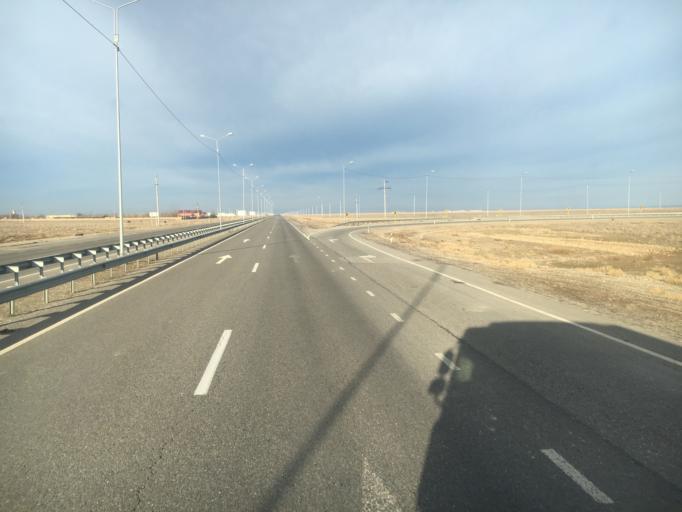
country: KZ
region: Ongtustik Qazaqstan
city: Turkestan
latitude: 43.4153
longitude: 68.0241
